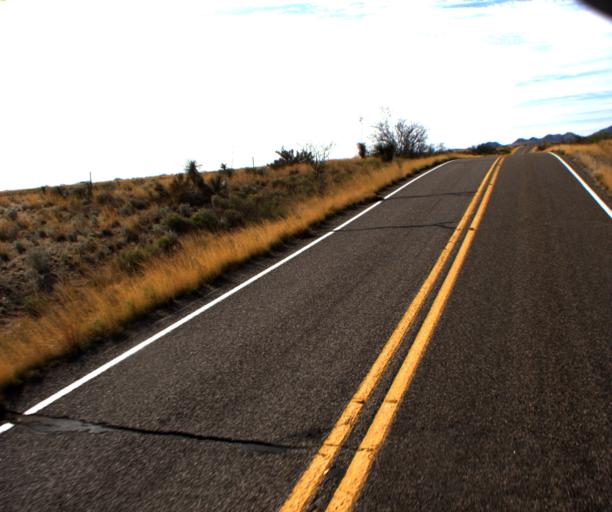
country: US
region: Arizona
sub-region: Cochise County
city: Willcox
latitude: 32.1005
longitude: -109.5417
